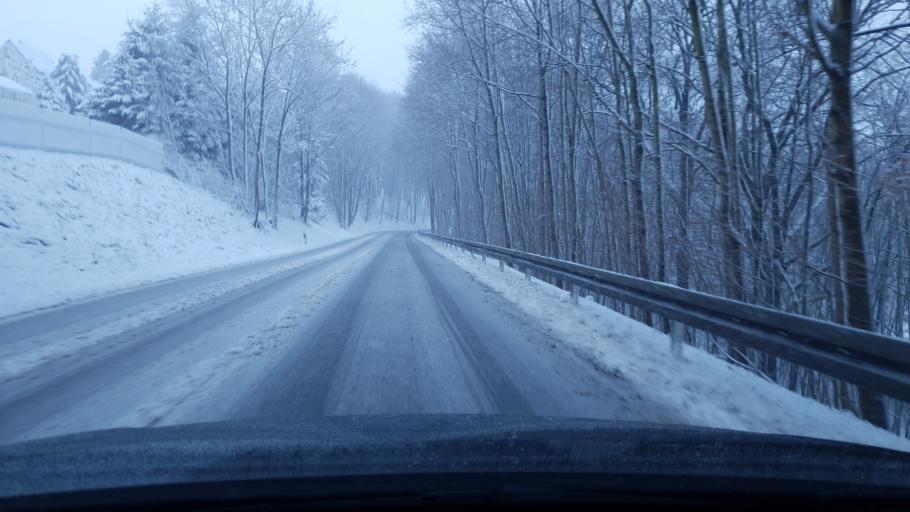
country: DE
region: Saxony
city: Wittgensdorf
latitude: 50.9015
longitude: 12.9000
